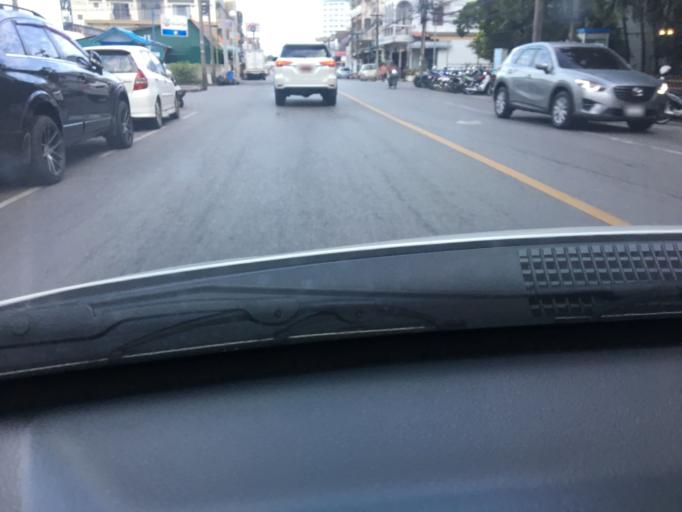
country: TH
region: Phuket
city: Ban Talat Yai
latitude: 7.8830
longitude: 98.3953
